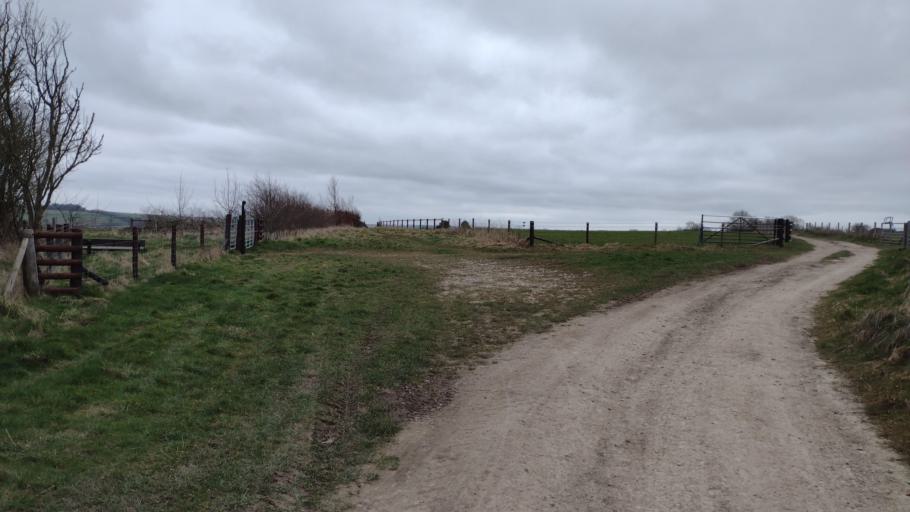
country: GB
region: England
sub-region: Wiltshire
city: Marlborough
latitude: 51.4542
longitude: -1.7561
